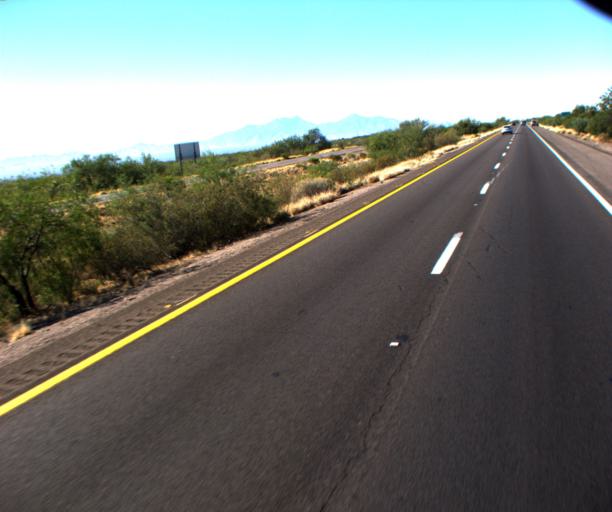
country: US
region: Arizona
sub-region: Pima County
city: Summit
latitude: 32.0208
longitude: -110.9926
